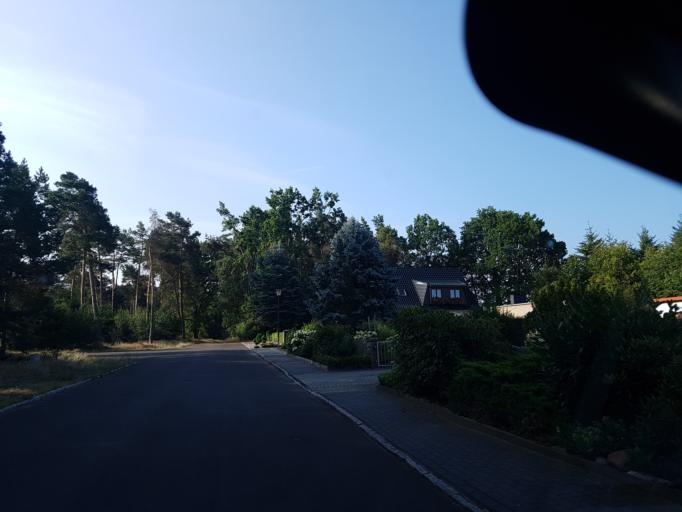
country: DE
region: Brandenburg
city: Niemegk
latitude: 52.0426
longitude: 12.7077
